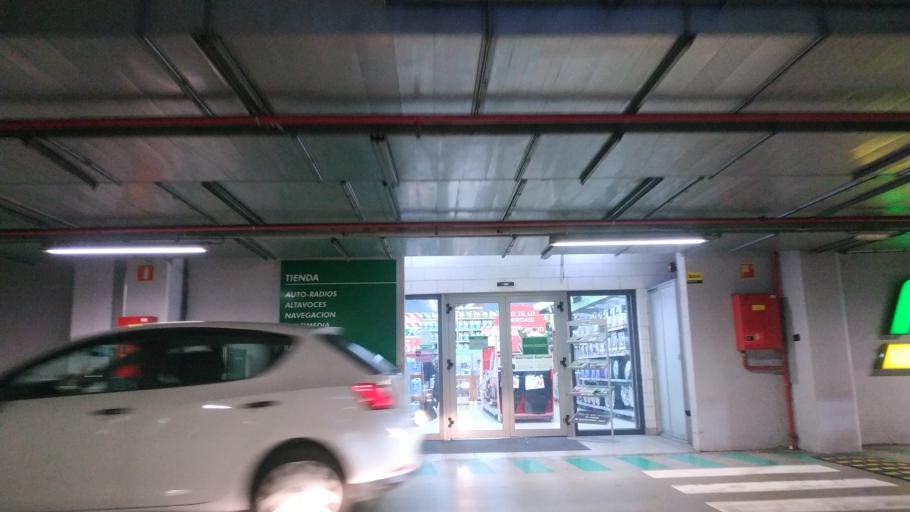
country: ES
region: Galicia
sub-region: Provincia da Coruna
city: A Coruna
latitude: 43.3442
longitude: -8.4272
